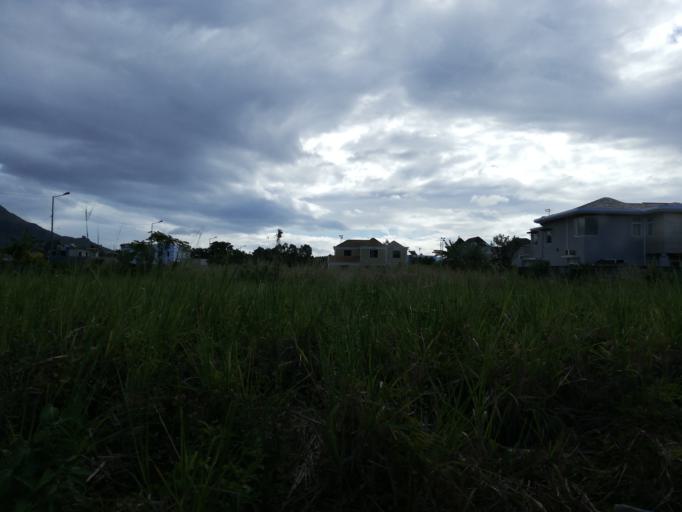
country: MU
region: Plaines Wilhems
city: Ebene
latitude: -20.2508
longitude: 57.4902
